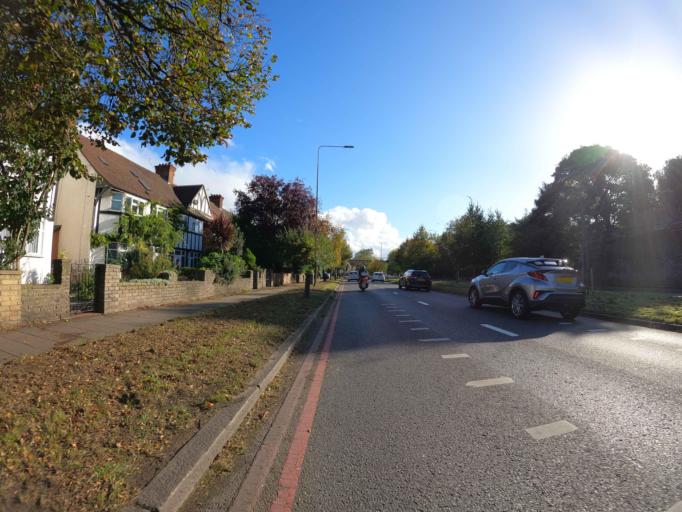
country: GB
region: England
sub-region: Greater London
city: Acton
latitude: 51.4984
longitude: -0.2825
